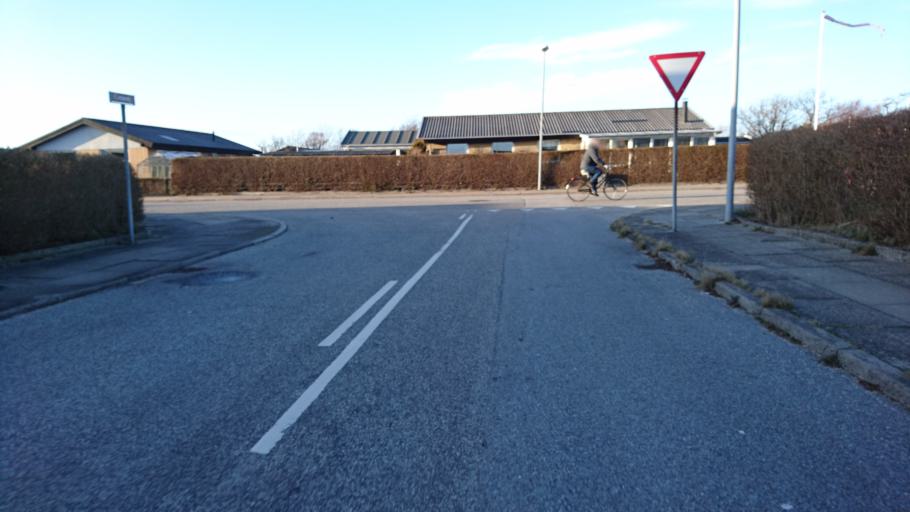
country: DK
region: North Denmark
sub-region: Frederikshavn Kommune
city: Skagen
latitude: 57.7304
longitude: 10.5915
